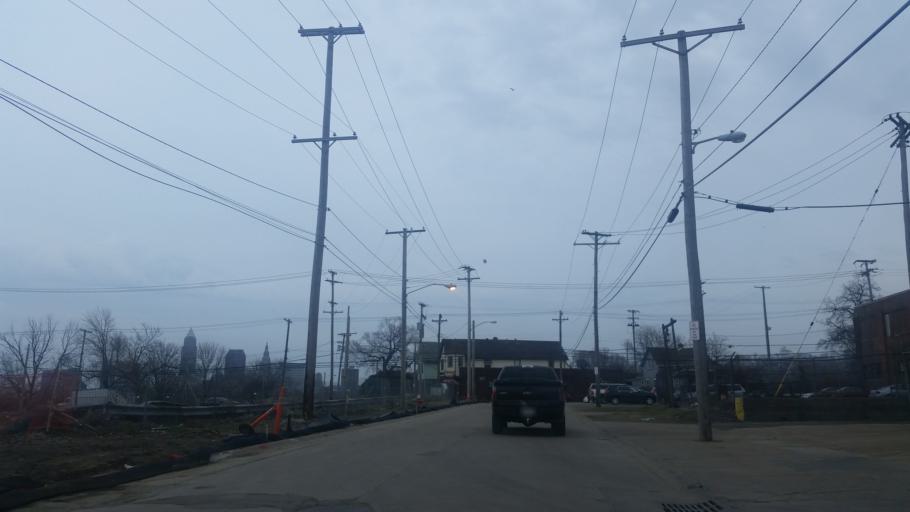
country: US
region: Ohio
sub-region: Cuyahoga County
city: Cleveland
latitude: 41.4887
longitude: -81.7274
